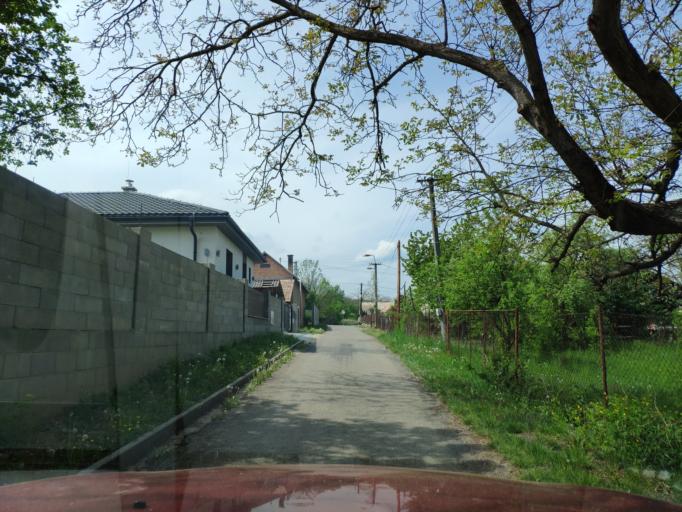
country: SK
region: Banskobystricky
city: Rimavska Sobota
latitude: 48.4797
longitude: 20.0728
